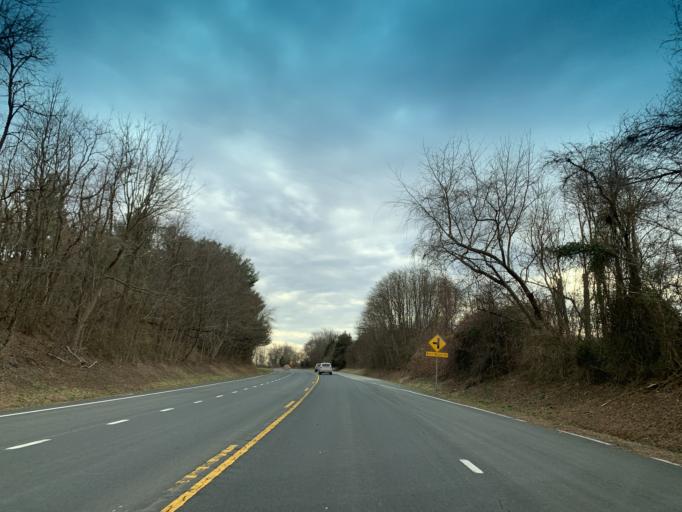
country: US
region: Maryland
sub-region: Washington County
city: Keedysville
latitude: 39.4228
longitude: -77.6635
